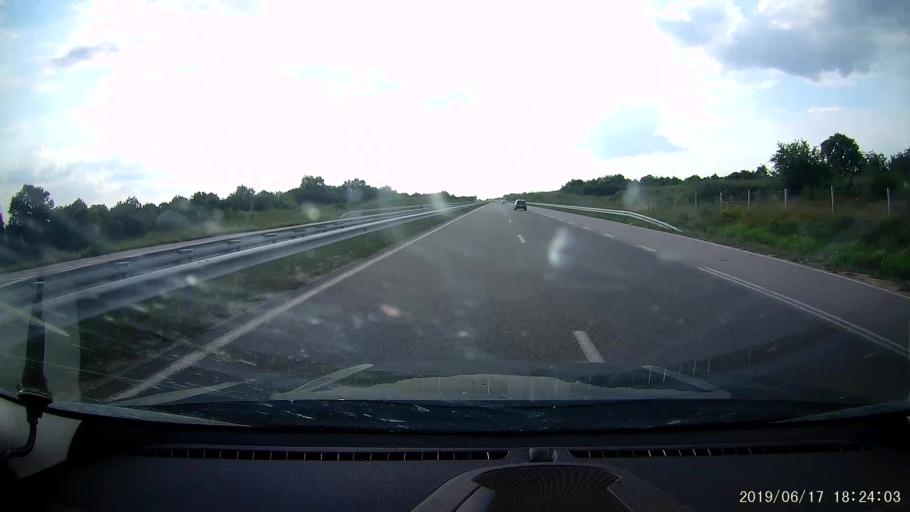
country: BG
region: Khaskovo
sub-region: Obshtina Dimitrovgrad
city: Dimitrovgrad
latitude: 41.9802
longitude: 25.7022
